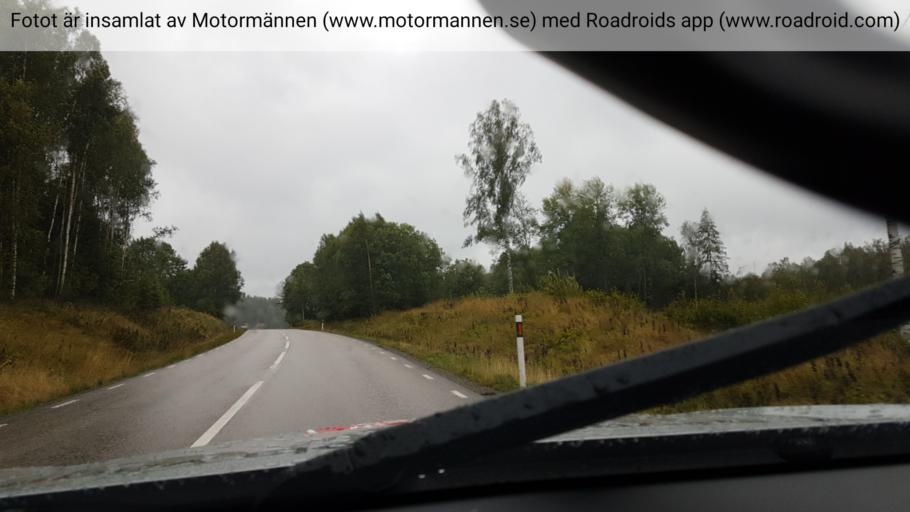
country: SE
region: Vaestra Goetaland
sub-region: Bengtsfors Kommun
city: Dals Langed
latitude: 58.8854
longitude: 12.2100
